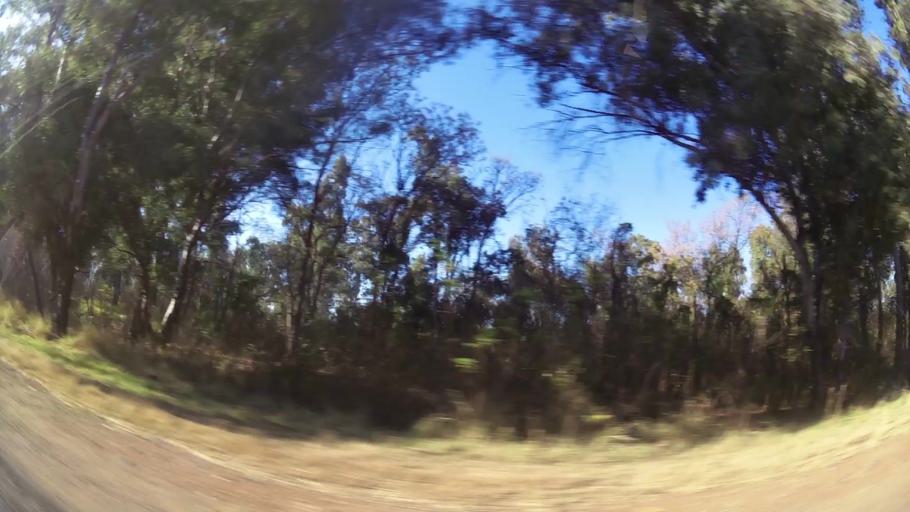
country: ZA
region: Gauteng
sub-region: City of Tshwane Metropolitan Municipality
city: Centurion
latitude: -25.8306
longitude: 28.1497
